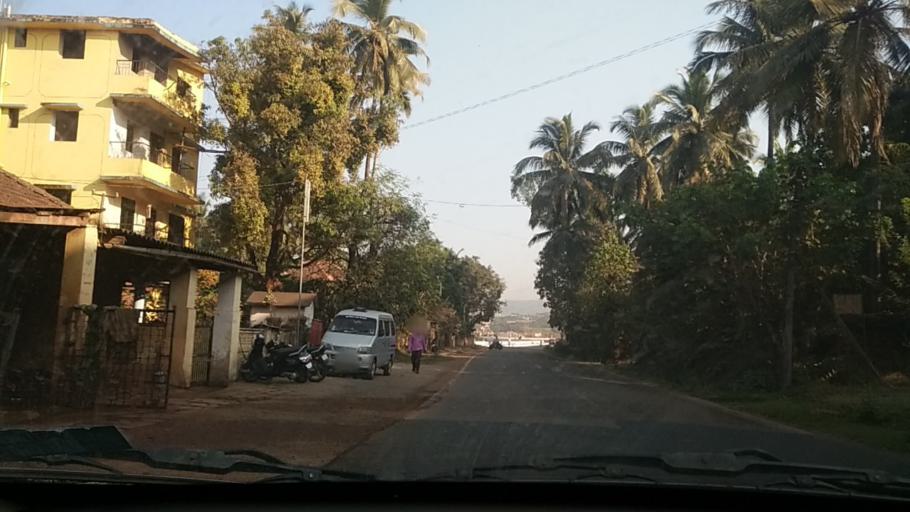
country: IN
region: Goa
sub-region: South Goa
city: Curchorem
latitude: 15.2565
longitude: 74.1044
